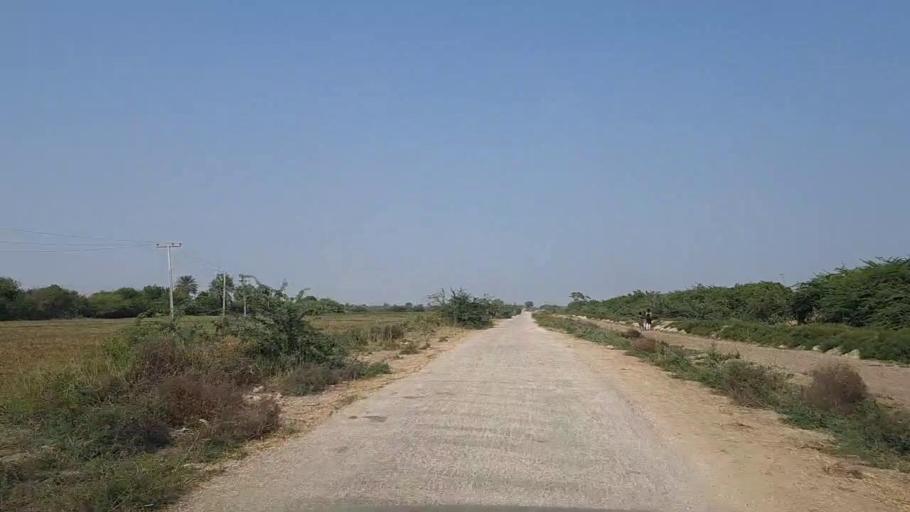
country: PK
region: Sindh
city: Chuhar Jamali
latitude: 24.5204
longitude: 67.9259
